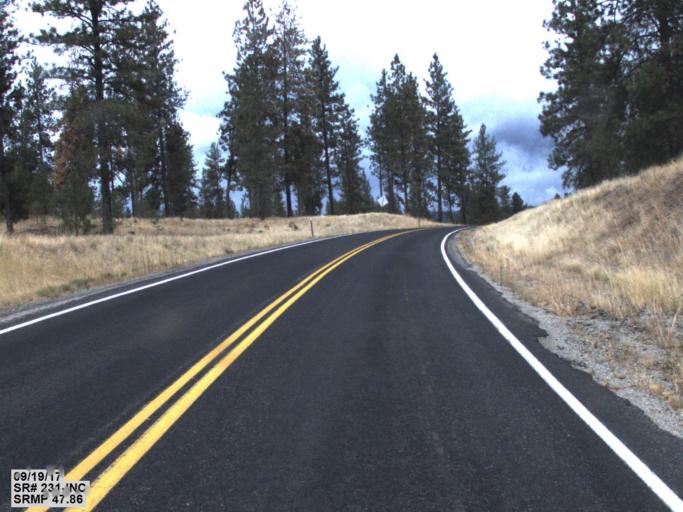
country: US
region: Washington
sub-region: Spokane County
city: Fairchild Air Force Base
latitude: 47.8804
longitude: -117.8396
